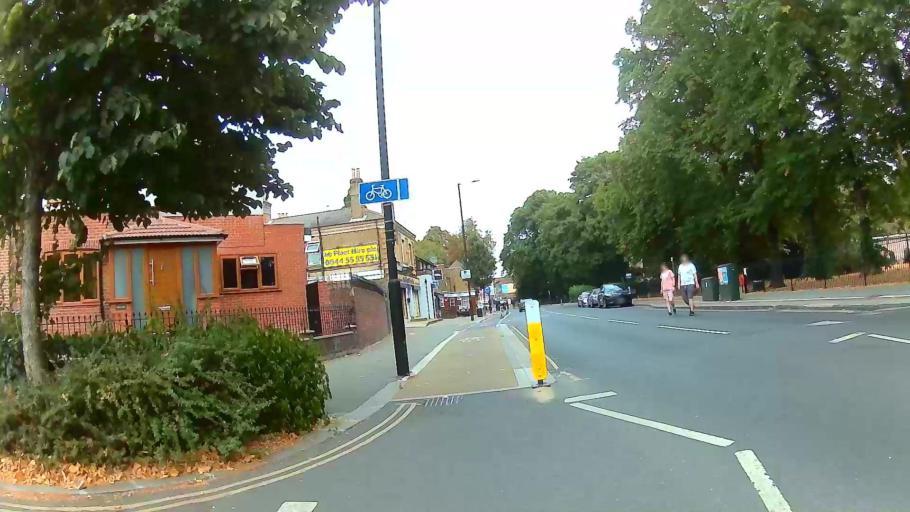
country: GB
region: England
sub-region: Greater London
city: Enfield
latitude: 51.6551
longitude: -0.0482
